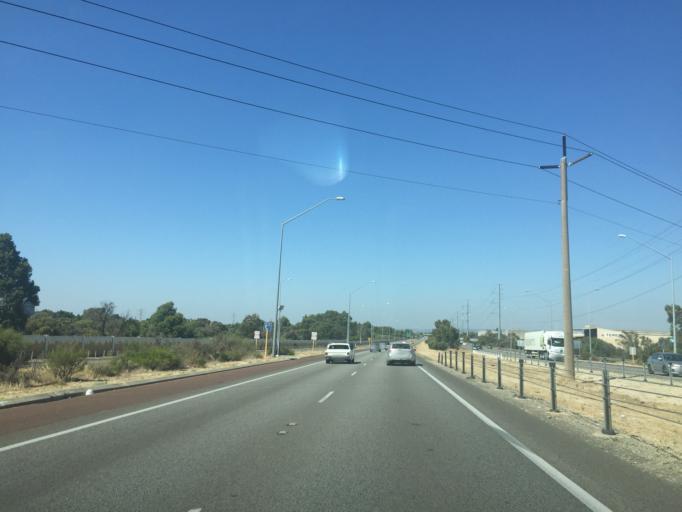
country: AU
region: Western Australia
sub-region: Canning
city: Willetton
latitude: -32.0670
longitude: 115.8922
